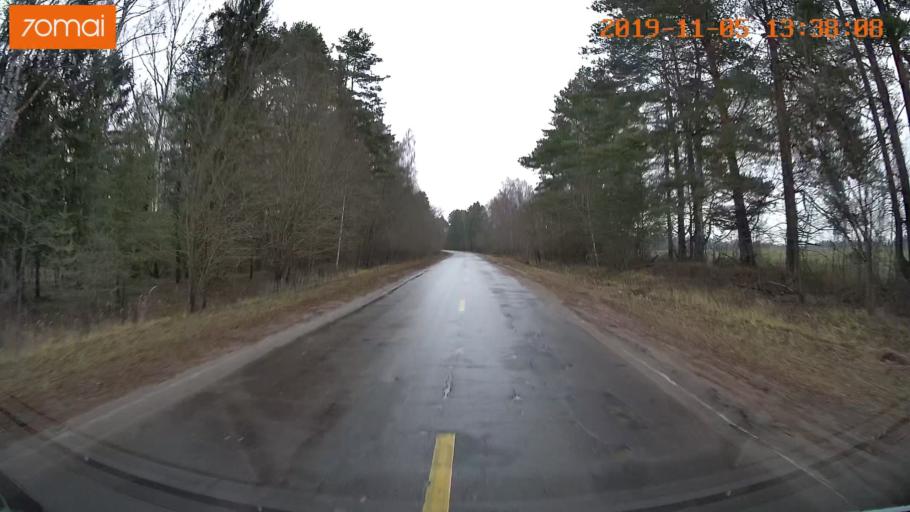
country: RU
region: Ivanovo
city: Shuya
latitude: 56.9290
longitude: 41.3842
